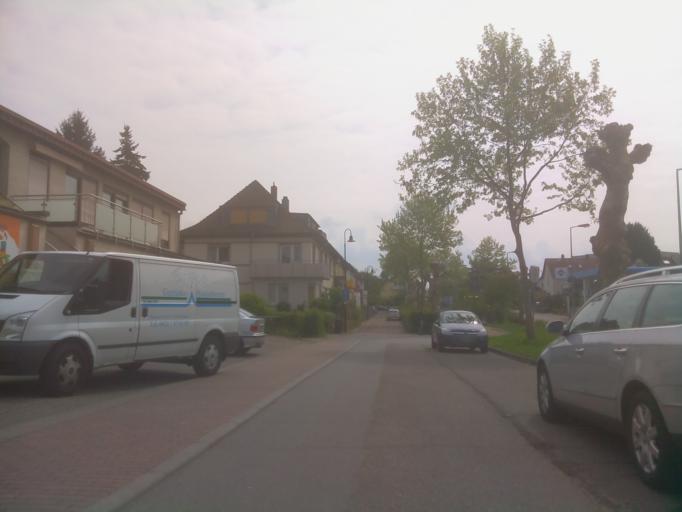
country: DE
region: Baden-Wuerttemberg
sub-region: Karlsruhe Region
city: Edingen-Neckarhausen
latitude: 49.4457
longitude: 8.5796
